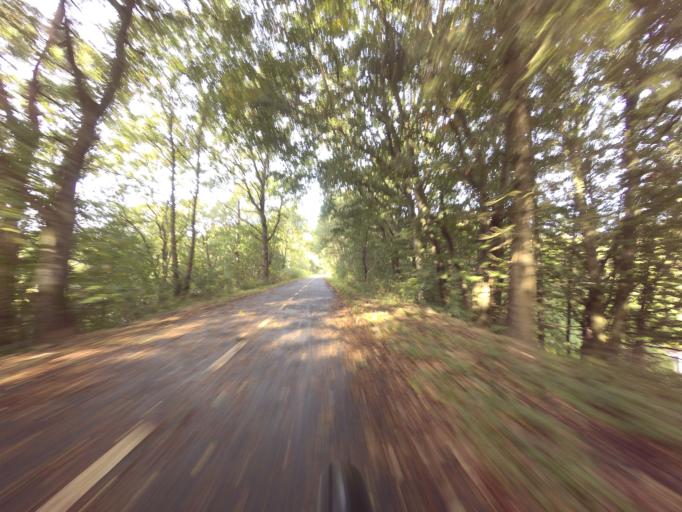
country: DK
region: Central Jutland
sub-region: Viborg Kommune
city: Viborg
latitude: 56.4229
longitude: 9.4362
